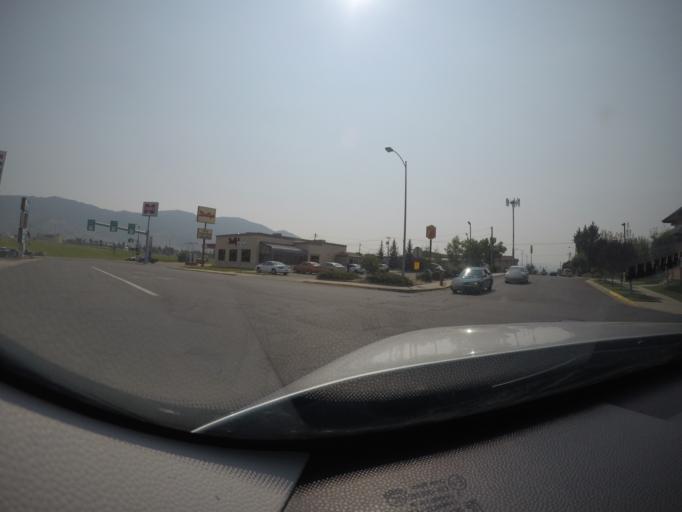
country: US
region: Montana
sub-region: Silver Bow County
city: Butte
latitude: 45.9835
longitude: -112.5095
